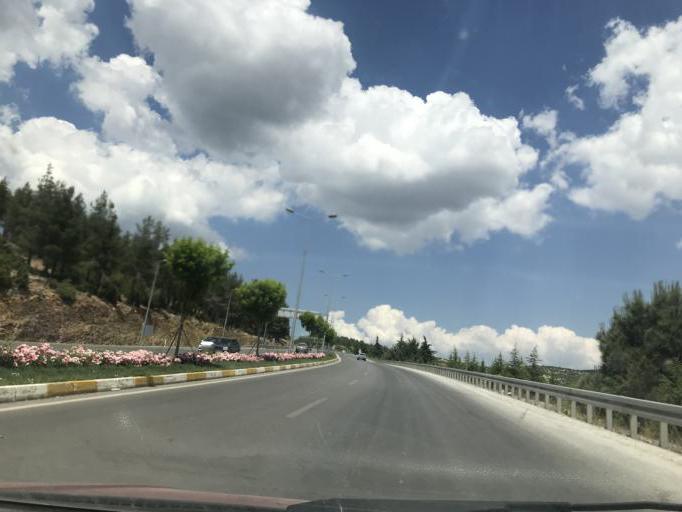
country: TR
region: Denizli
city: Tavas
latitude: 37.5739
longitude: 29.0838
